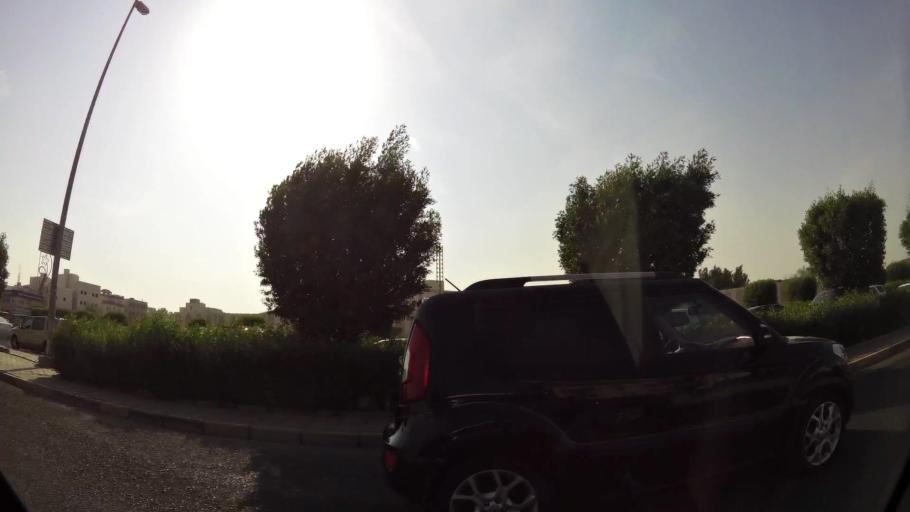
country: KW
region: Mubarak al Kabir
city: Mubarak al Kabir
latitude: 29.1853
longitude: 48.0806
